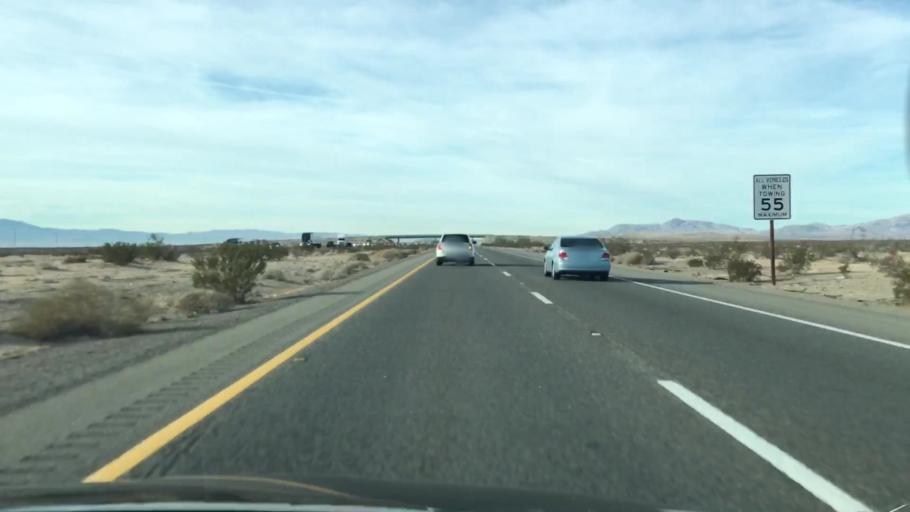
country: US
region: California
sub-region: San Bernardino County
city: Fort Irwin
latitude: 34.9875
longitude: -116.5908
